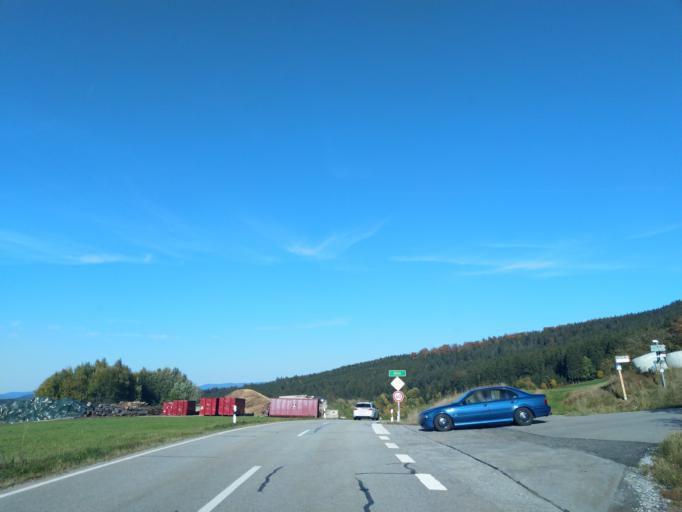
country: DE
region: Bavaria
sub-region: Lower Bavaria
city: Achslach
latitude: 48.9415
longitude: 12.9227
